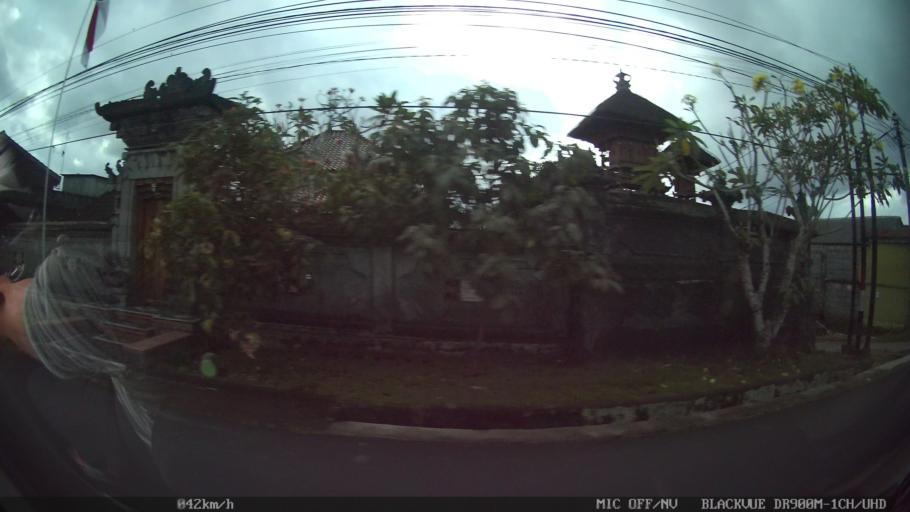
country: ID
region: Bali
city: Banjar Tegal Belodan
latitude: -8.5426
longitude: 115.1167
